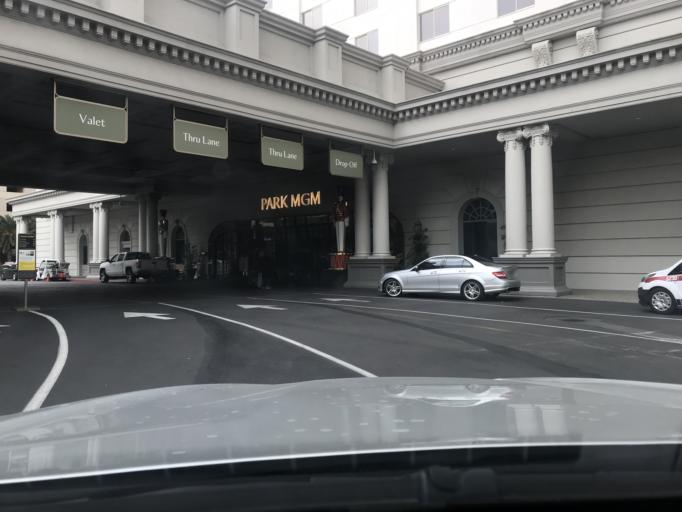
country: US
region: Nevada
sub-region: Clark County
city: Paradise
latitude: 36.1045
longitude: -115.1764
